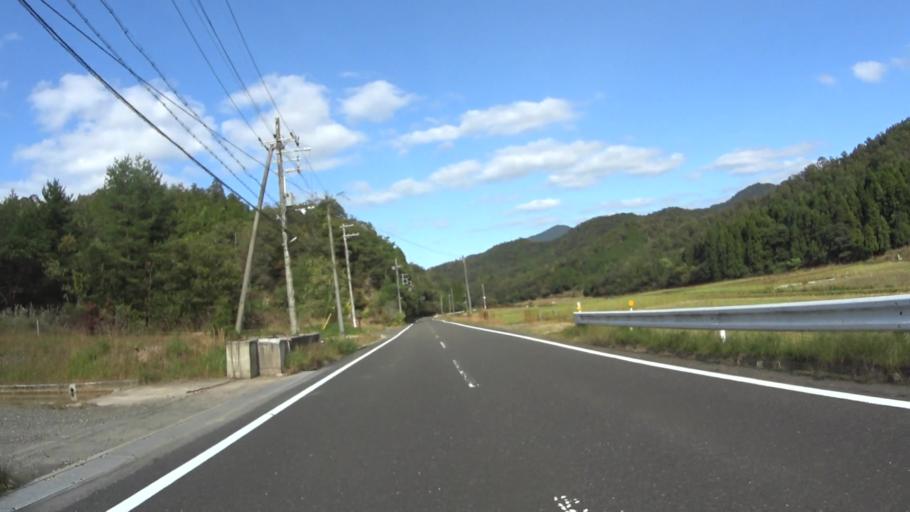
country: JP
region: Hyogo
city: Toyooka
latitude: 35.5534
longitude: 134.9773
